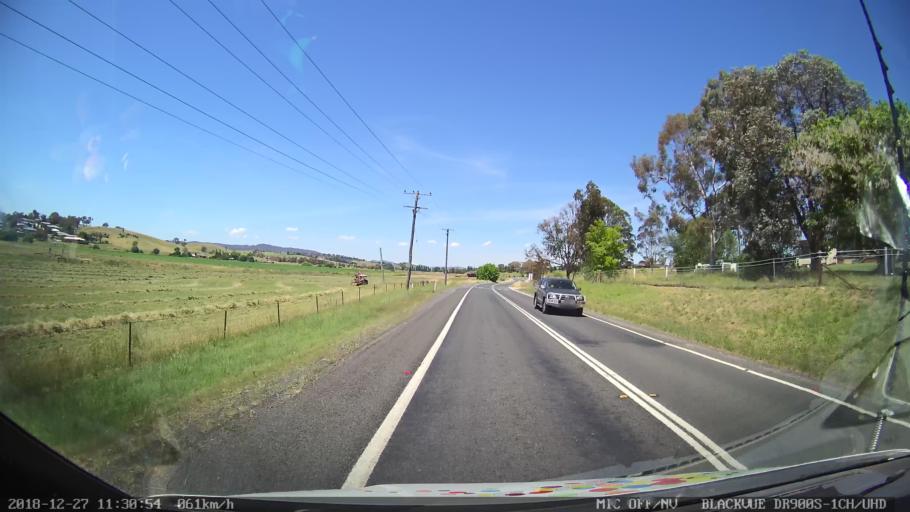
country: AU
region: New South Wales
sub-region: Bathurst Regional
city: Perthville
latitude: -33.4900
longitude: 149.5421
